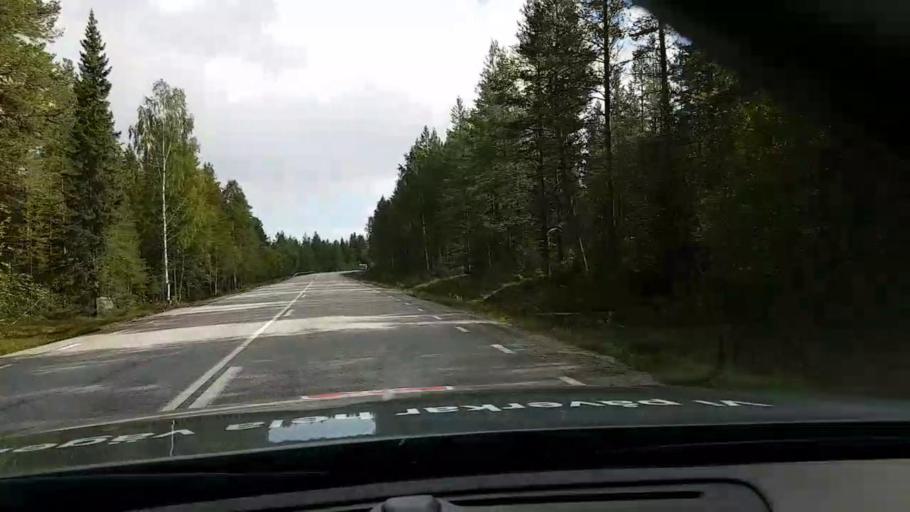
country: SE
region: Vaesternorrland
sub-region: OErnskoeldsviks Kommun
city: Bredbyn
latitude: 63.6353
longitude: 17.9057
